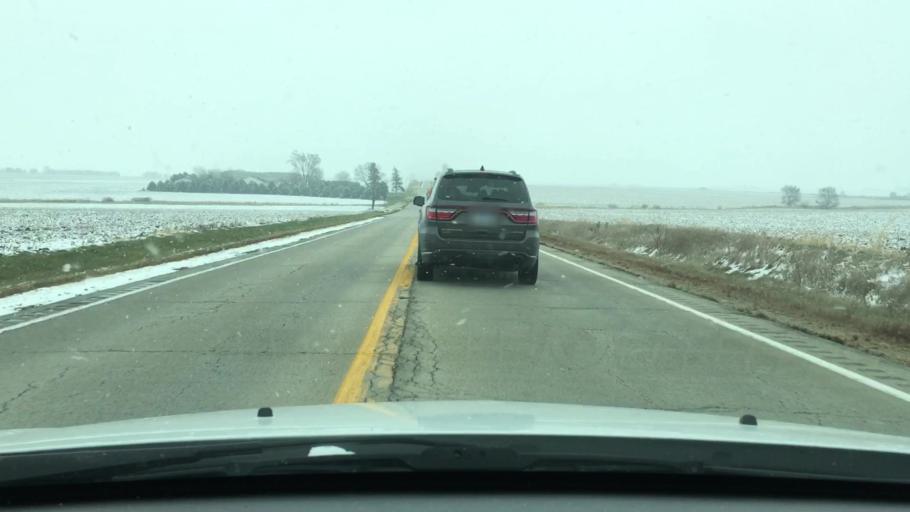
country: US
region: Illinois
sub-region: DeKalb County
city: Malta
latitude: 41.9355
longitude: -88.9381
